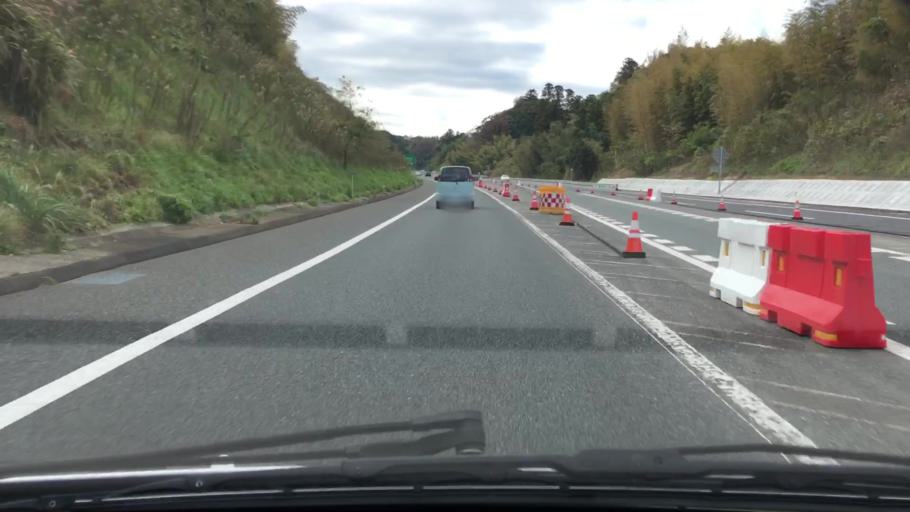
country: JP
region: Chiba
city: Kimitsu
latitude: 35.2605
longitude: 139.8968
